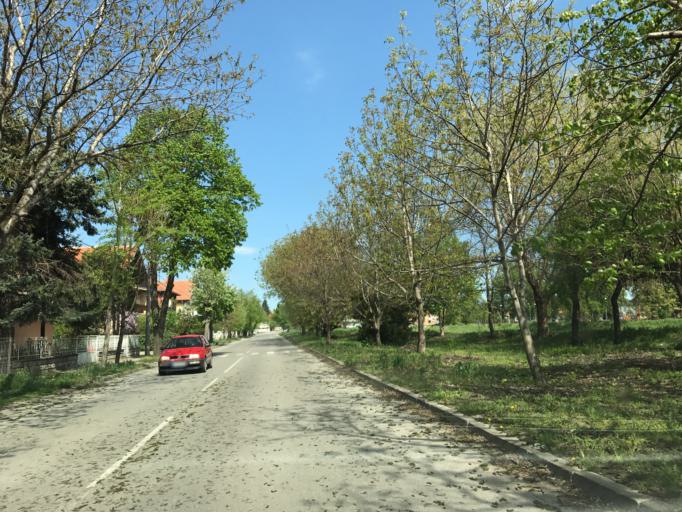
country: RS
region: Central Serbia
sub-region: Zajecarski Okrug
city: Zajecar
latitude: 43.9110
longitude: 22.2715
